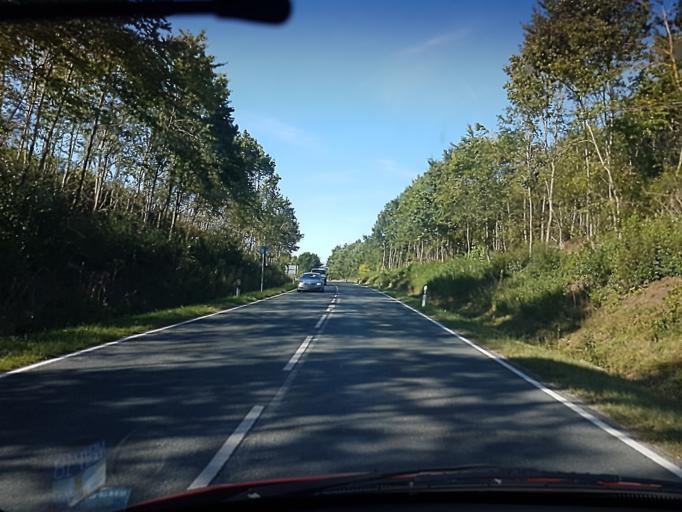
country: DE
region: Bavaria
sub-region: Regierungsbezirk Mittelfranken
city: Adelsdorf
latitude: 49.7011
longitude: 10.9144
